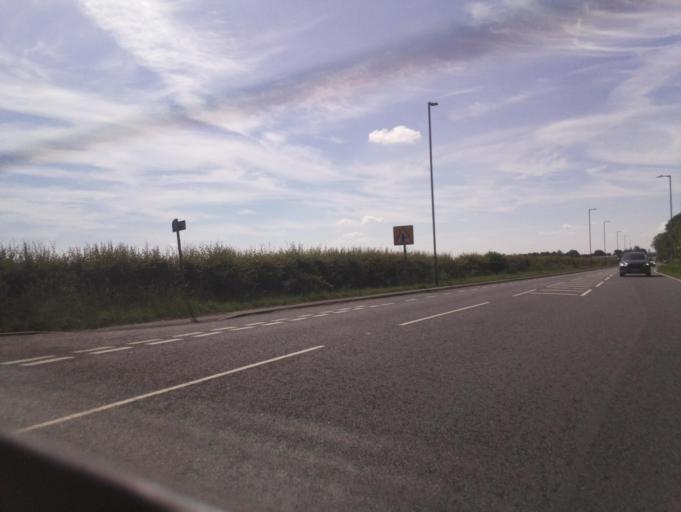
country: GB
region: England
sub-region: Lincolnshire
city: Burton
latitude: 53.2988
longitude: -0.5413
